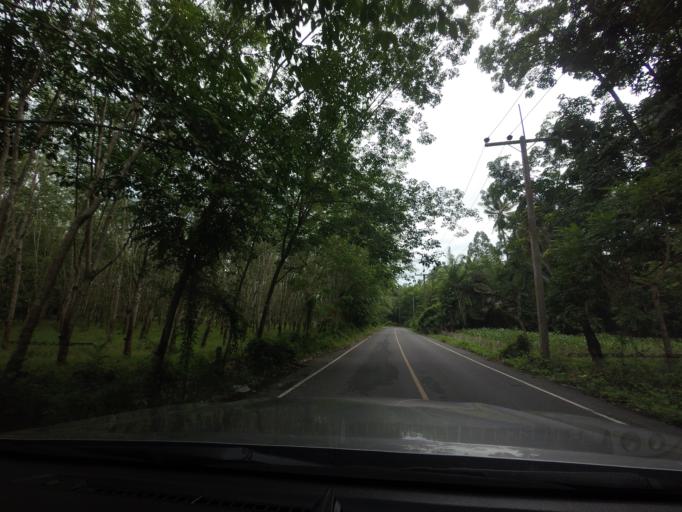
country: TH
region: Nakhon Si Thammarat
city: Phra Phrom
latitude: 8.2801
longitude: 99.9406
